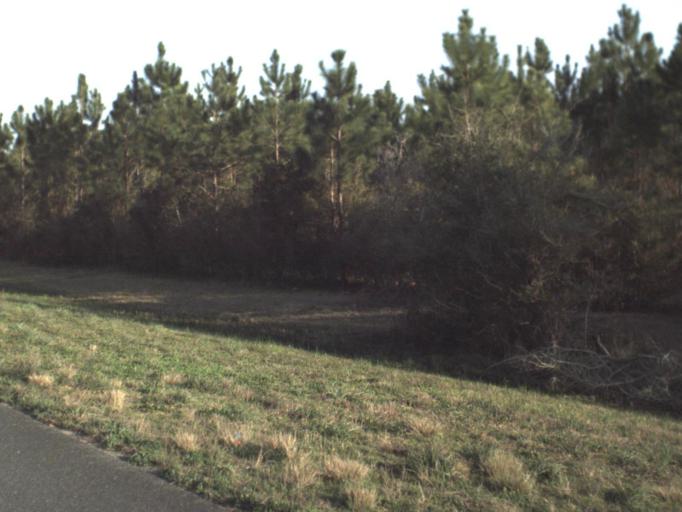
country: US
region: Florida
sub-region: Bay County
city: Lynn Haven
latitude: 30.4391
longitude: -85.7281
